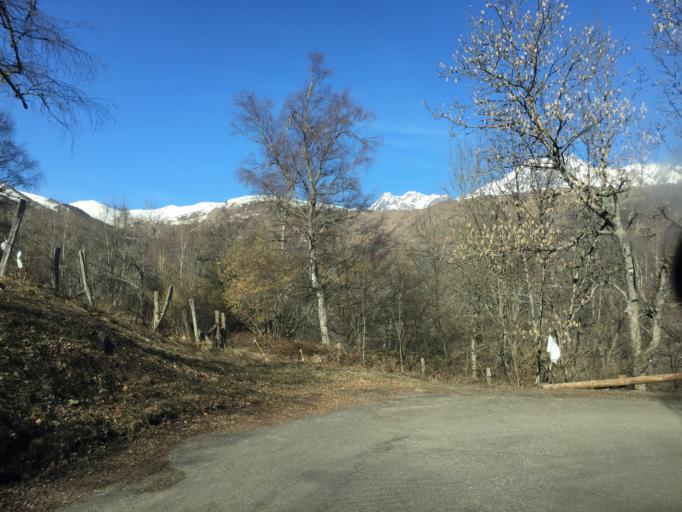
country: FR
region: Midi-Pyrenees
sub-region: Departement des Hautes-Pyrenees
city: Saint-Lary-Soulan
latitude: 42.8134
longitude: 0.3355
